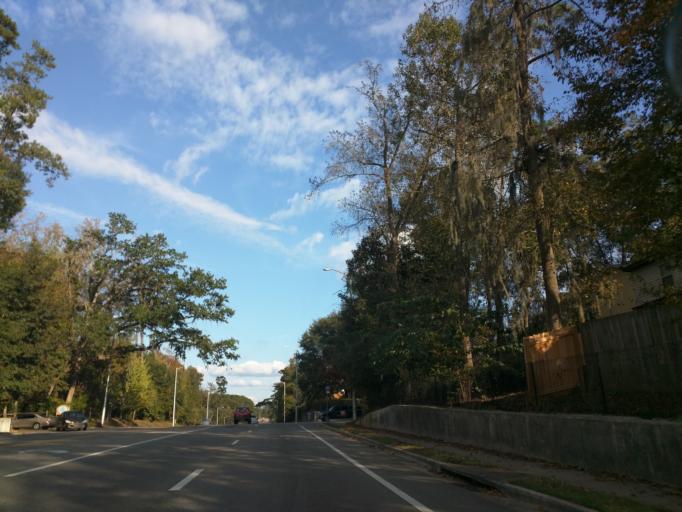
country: US
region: Florida
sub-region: Leon County
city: Tallahassee
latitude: 30.4418
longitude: -84.2373
